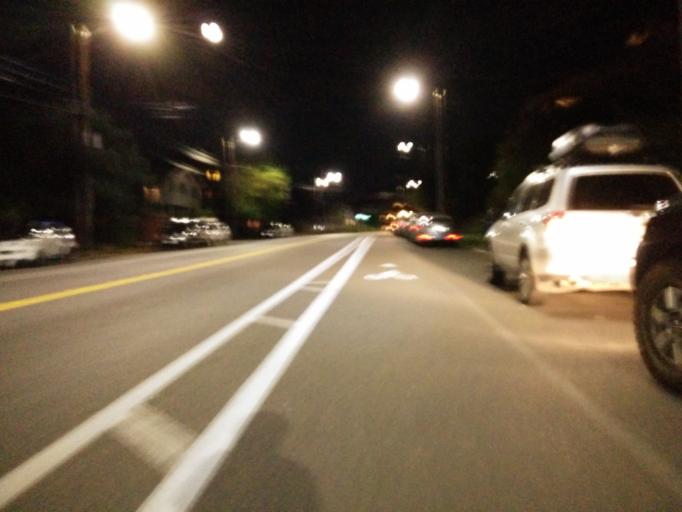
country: US
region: Washington
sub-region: King County
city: Seattle
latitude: 47.6430
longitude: -122.3454
